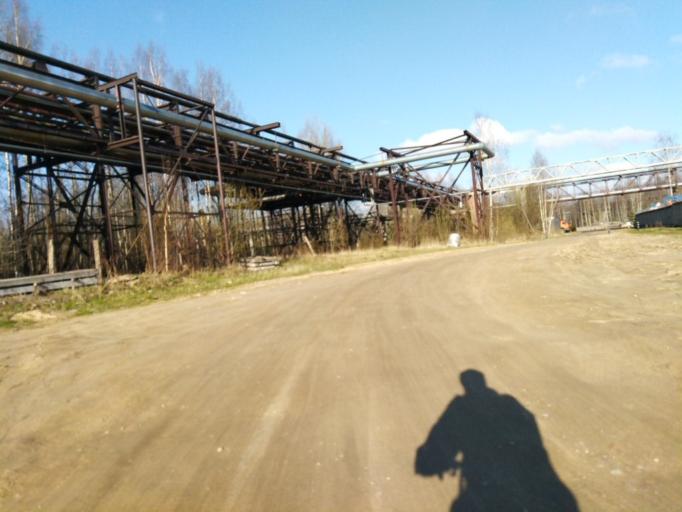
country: RU
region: Leningrad
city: Novoye Devyatkino
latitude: 60.0721
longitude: 30.4770
